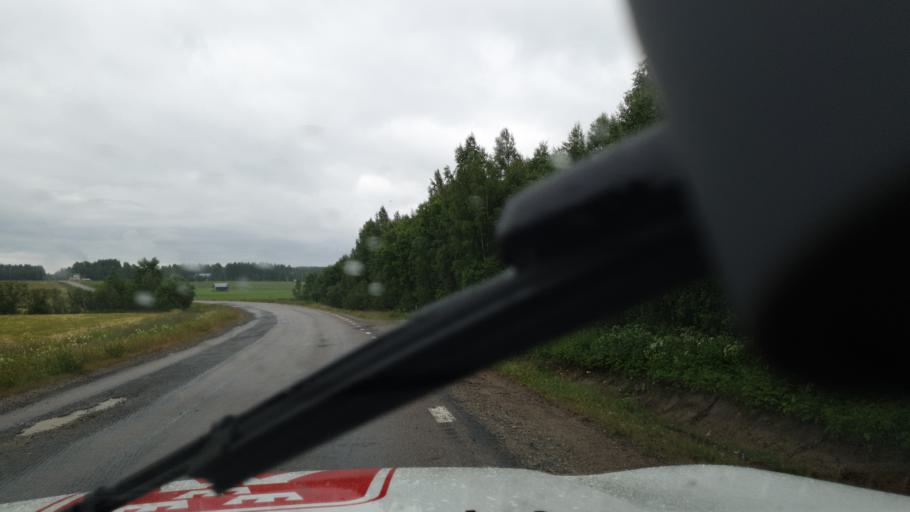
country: SE
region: Vaesterbotten
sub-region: Vannas Kommun
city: Vannasby
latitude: 63.7779
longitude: 19.8501
